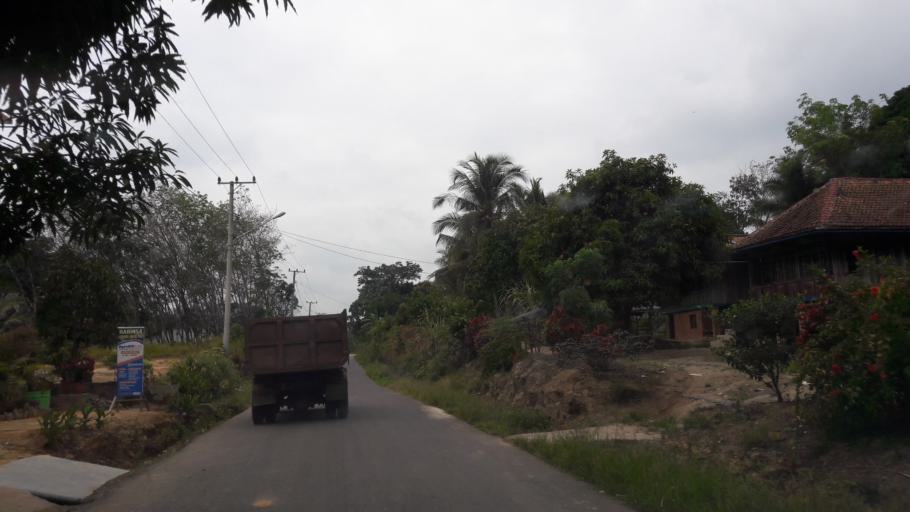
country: ID
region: South Sumatra
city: Gunungmenang
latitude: -3.2134
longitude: 103.9858
